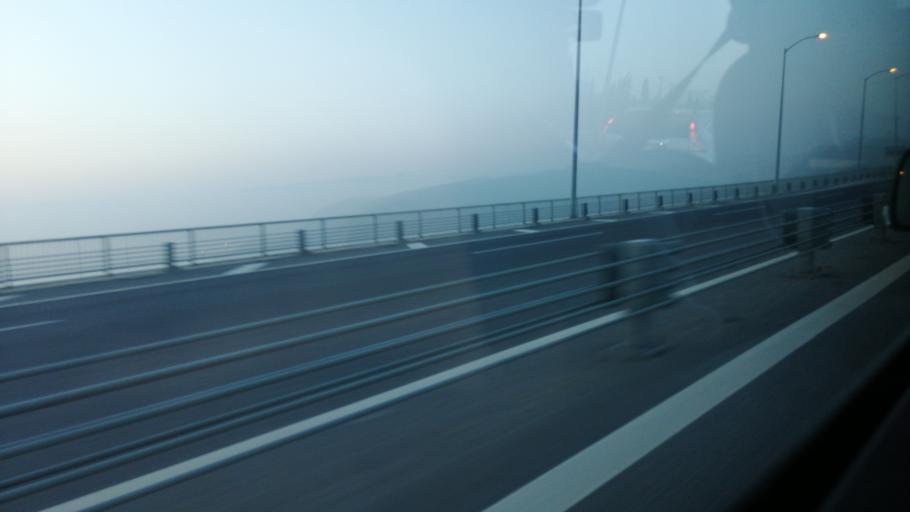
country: TR
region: Kocaeli
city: Tavsanli
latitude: 40.7691
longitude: 29.5182
